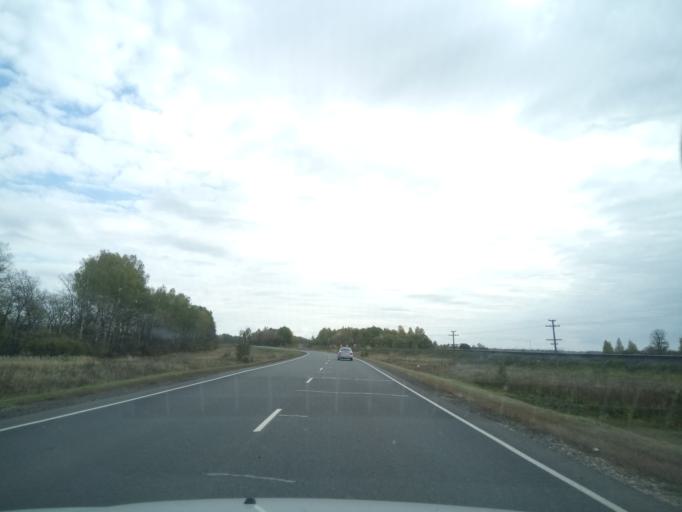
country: RU
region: Nizjnij Novgorod
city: Lukoyanov
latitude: 55.0662
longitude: 44.3482
